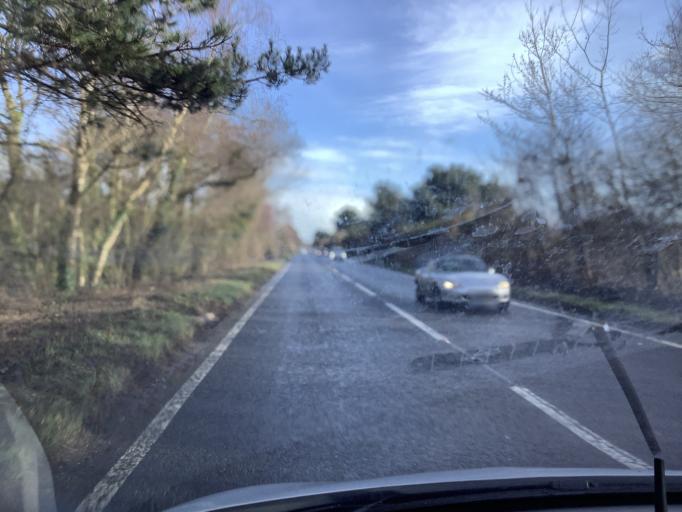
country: GB
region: England
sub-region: Hampshire
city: Hythe
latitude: 50.8462
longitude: -1.4036
